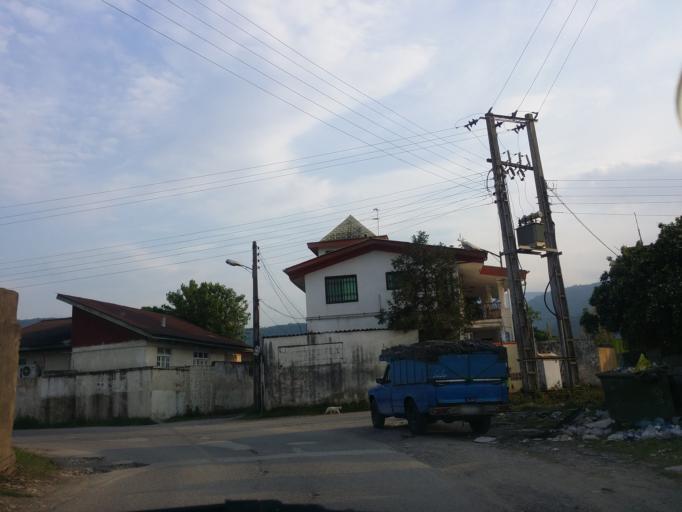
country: IR
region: Mazandaran
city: Chalus
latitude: 36.6640
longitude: 51.3749
